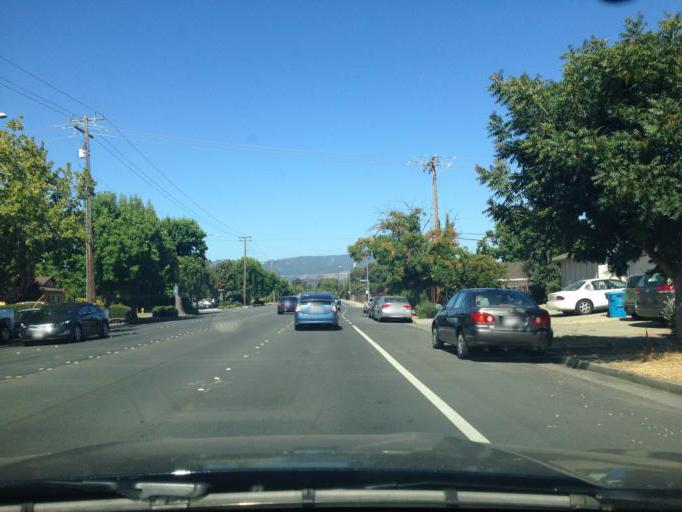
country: US
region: California
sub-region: Santa Clara County
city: Cupertino
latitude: 37.3102
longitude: -122.0167
